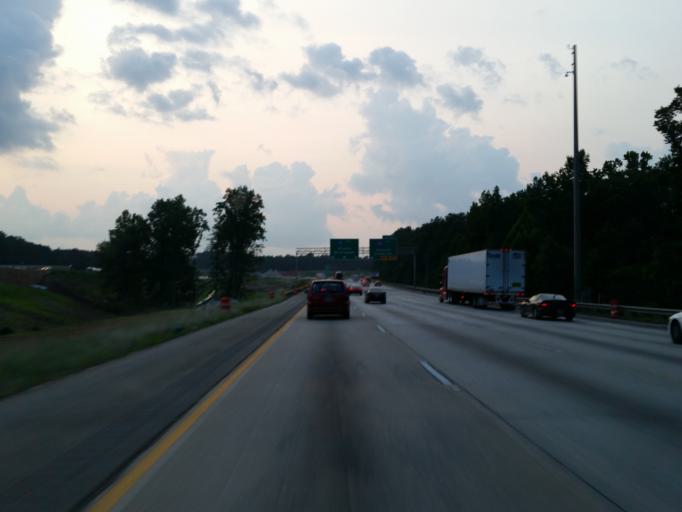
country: US
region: Georgia
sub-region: Henry County
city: Stockbridge
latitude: 33.5377
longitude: -84.2636
